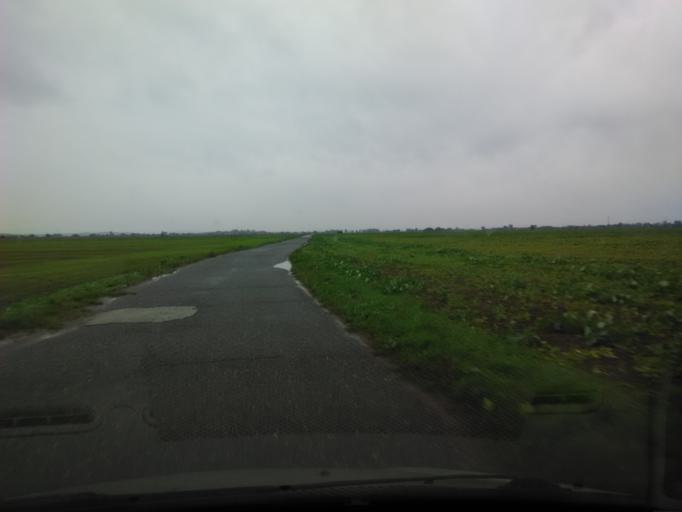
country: SK
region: Nitriansky
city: Tlmace
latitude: 48.2648
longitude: 18.5423
